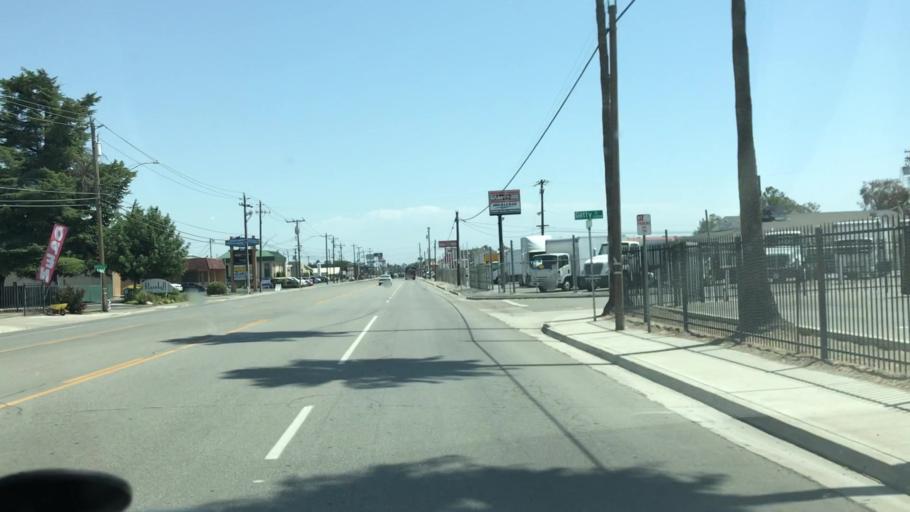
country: US
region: California
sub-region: Kern County
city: Bakersfield
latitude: 35.3936
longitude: -119.0433
